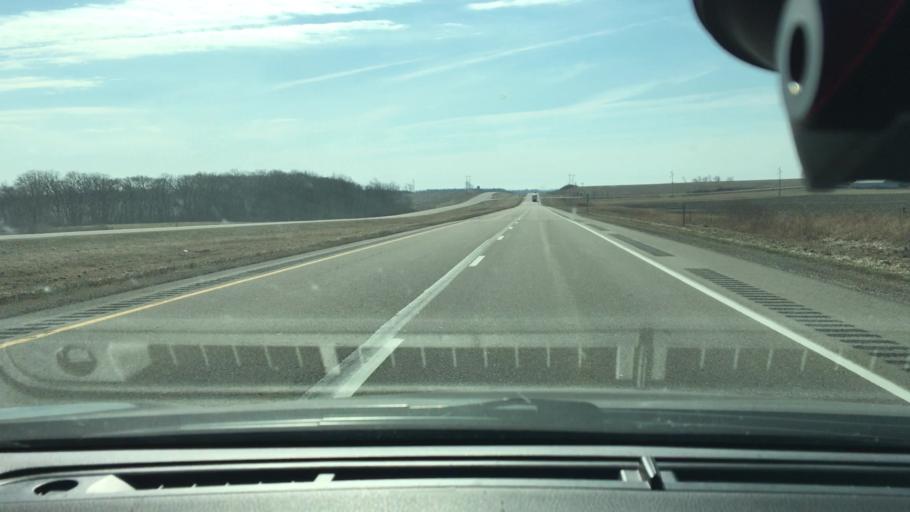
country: US
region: Iowa
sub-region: Floyd County
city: Charles City
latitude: 43.0054
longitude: -92.6191
